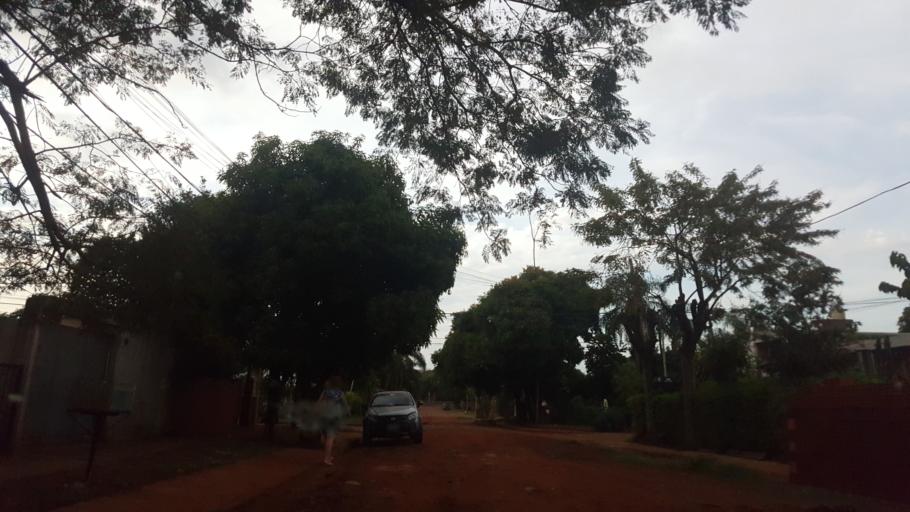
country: AR
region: Misiones
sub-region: Departamento de Capital
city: Posadas
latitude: -27.3912
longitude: -55.9170
